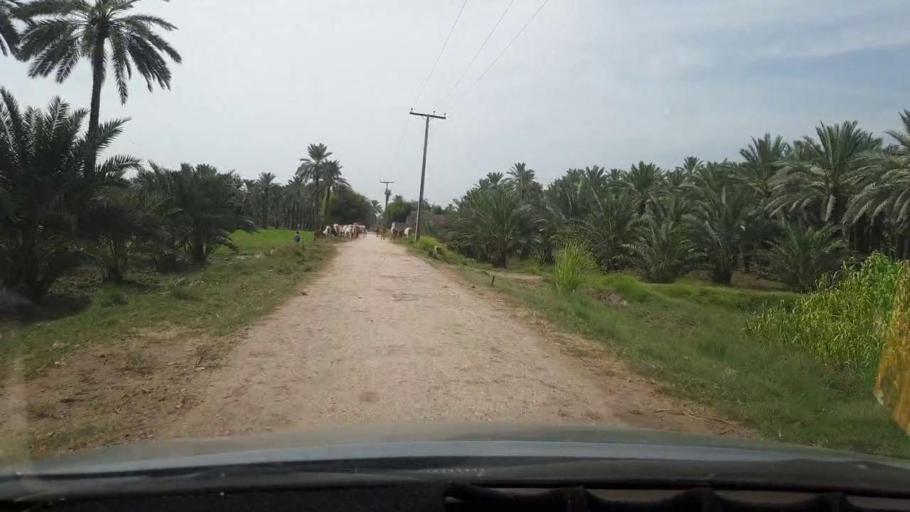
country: PK
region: Sindh
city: Khairpur
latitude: 27.4951
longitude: 68.7545
